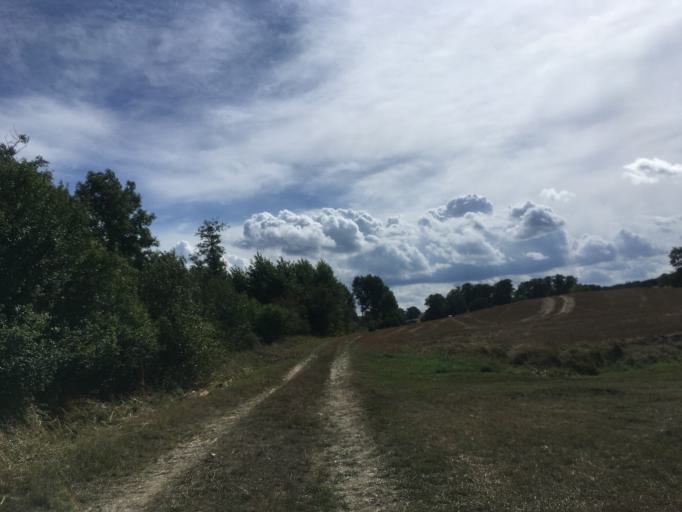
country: DE
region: Brandenburg
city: Gerswalde
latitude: 53.1319
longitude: 13.7848
